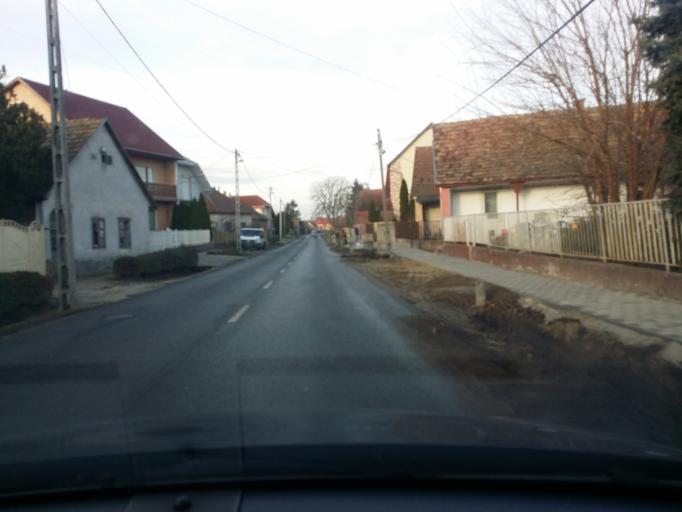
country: HU
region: Pest
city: Alsonemedi
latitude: 47.3163
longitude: 19.1598
